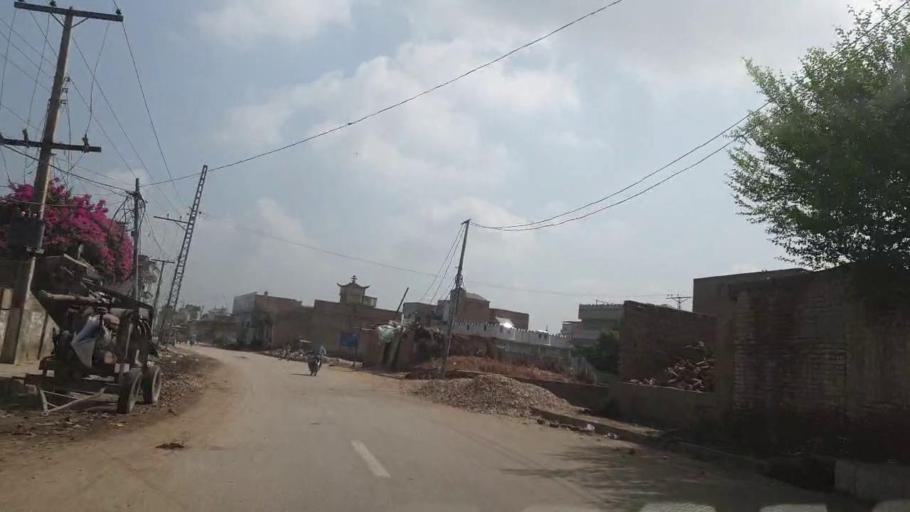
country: PK
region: Sindh
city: Khairpur
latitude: 27.5329
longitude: 68.7501
